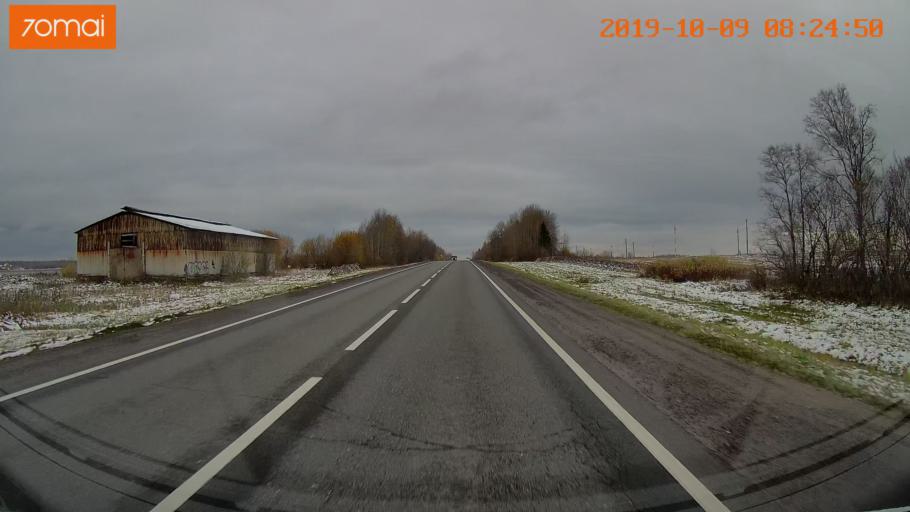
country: RU
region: Vologda
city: Gryazovets
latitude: 58.7720
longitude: 40.2760
